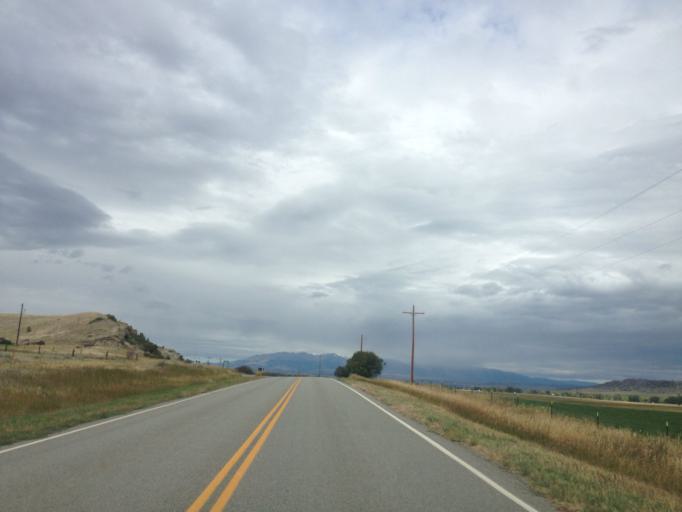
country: US
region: Montana
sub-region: Sweet Grass County
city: Big Timber
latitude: 45.7774
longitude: -109.8098
